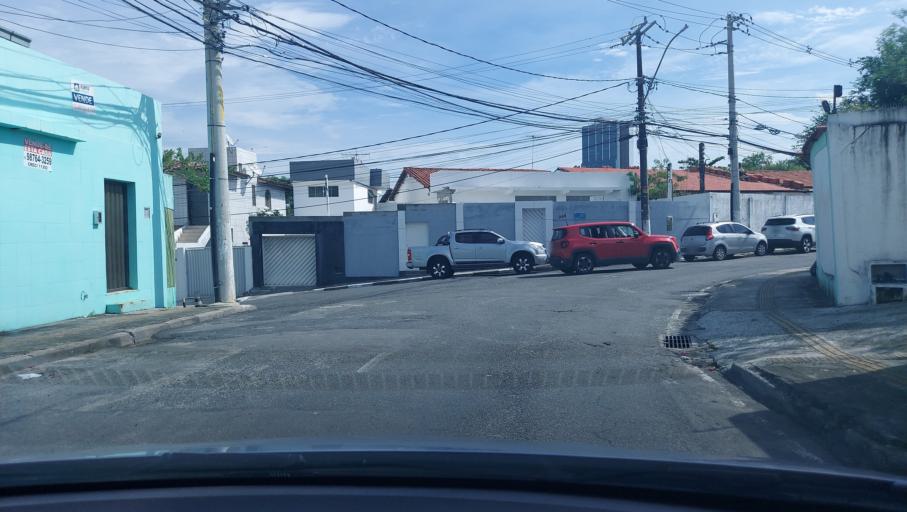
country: BR
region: Bahia
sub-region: Salvador
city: Salvador
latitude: -12.9824
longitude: -38.4461
